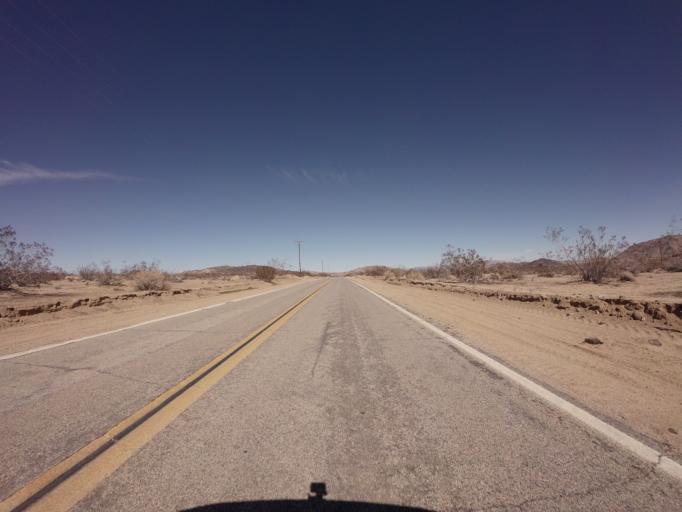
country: US
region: California
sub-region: San Bernardino County
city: Yucca Valley
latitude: 34.2801
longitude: -116.4045
